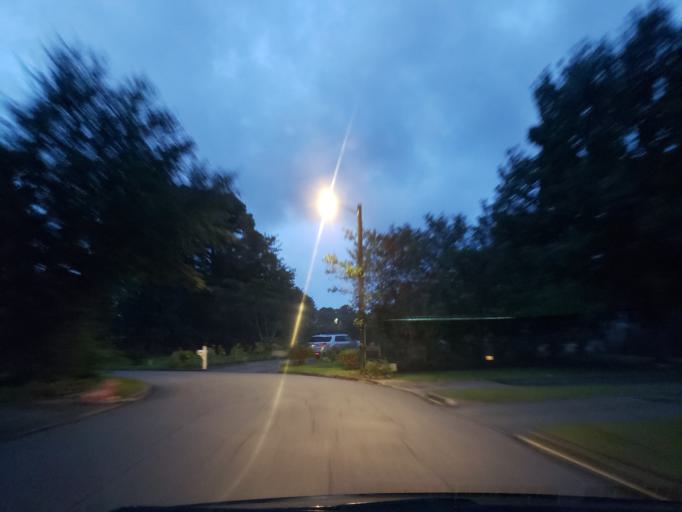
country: US
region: Georgia
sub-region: Chatham County
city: Isle of Hope
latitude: 31.9858
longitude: -81.0768
